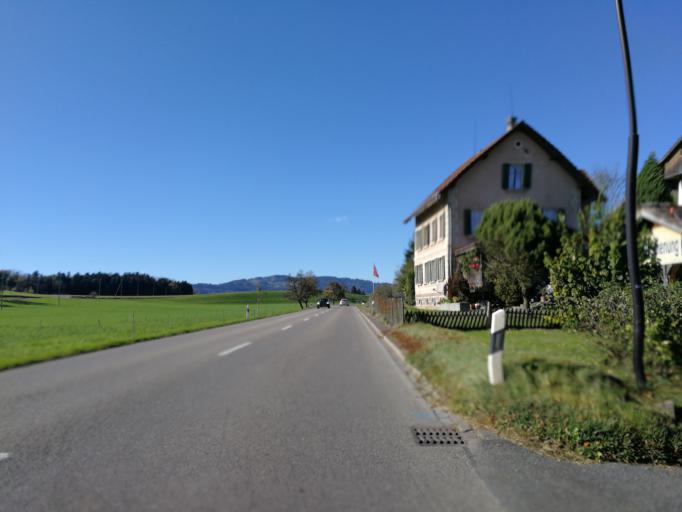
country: CH
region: Zurich
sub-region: Bezirk Hinwil
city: Binzikon
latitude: 47.2851
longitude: 8.7517
